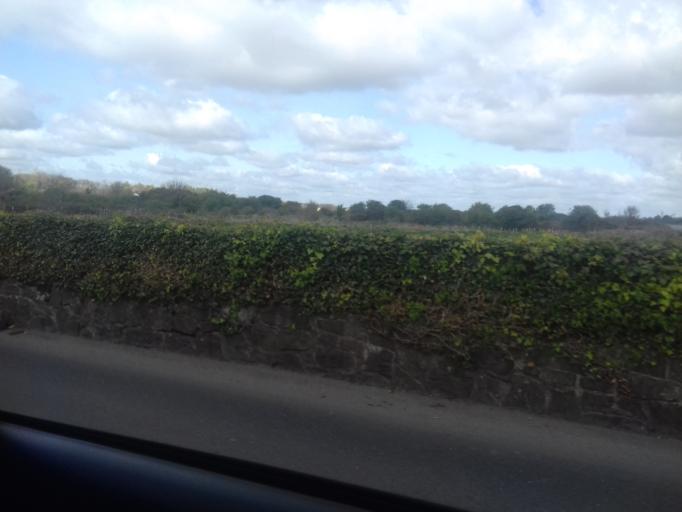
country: IE
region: Leinster
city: Malahide
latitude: 53.4550
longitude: -6.1688
